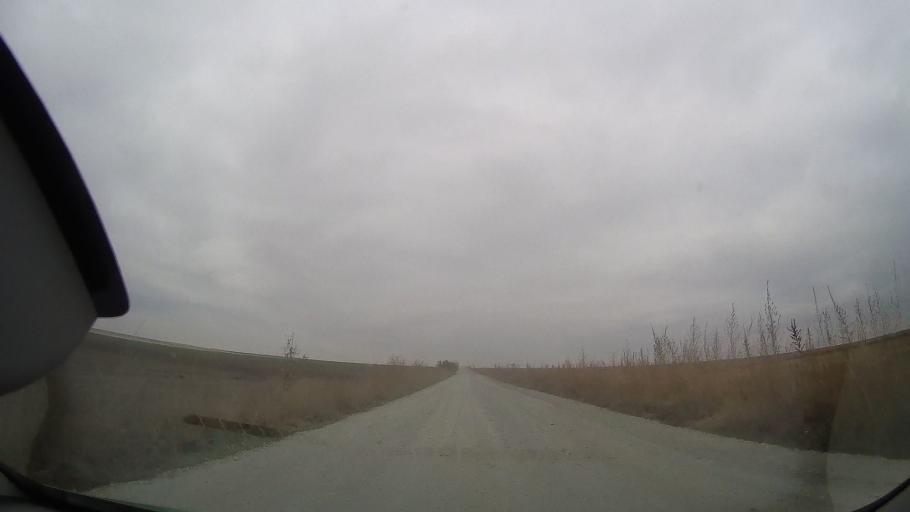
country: RO
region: Ialomita
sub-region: Comuna Grivita
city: Grivita
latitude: 44.7484
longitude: 27.2667
